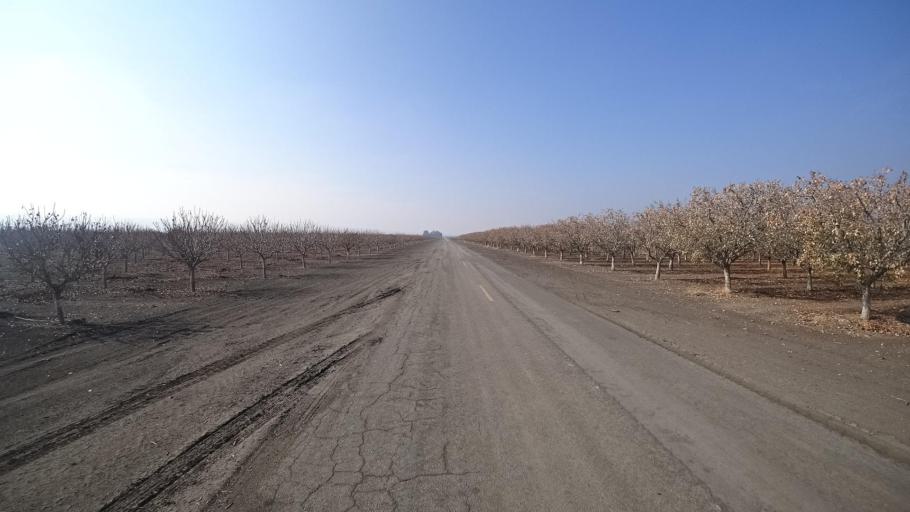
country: US
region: California
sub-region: Kern County
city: Buttonwillow
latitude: 35.3402
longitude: -119.4126
